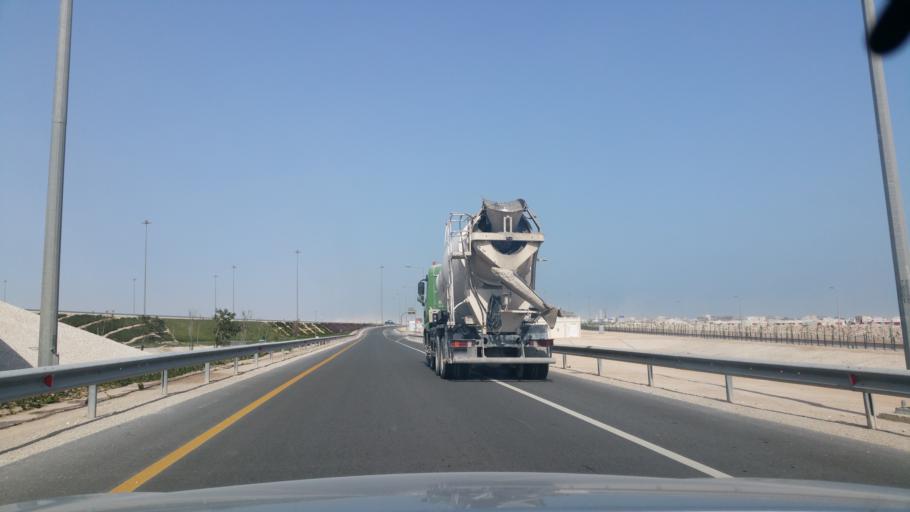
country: QA
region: Baladiyat az Za`ayin
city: Az Za`ayin
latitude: 25.5674
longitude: 51.4612
